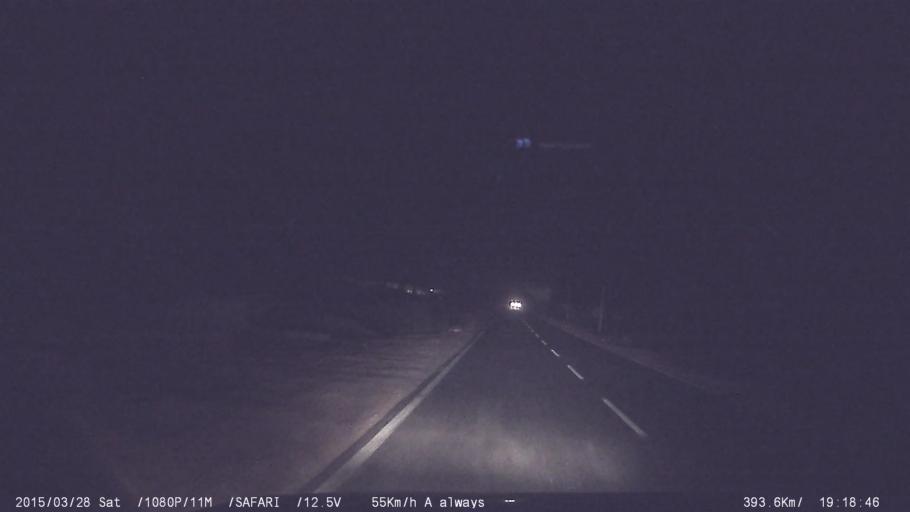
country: IN
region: Karnataka
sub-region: Mandya
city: Shrirangapattana
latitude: 12.4088
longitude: 76.6565
